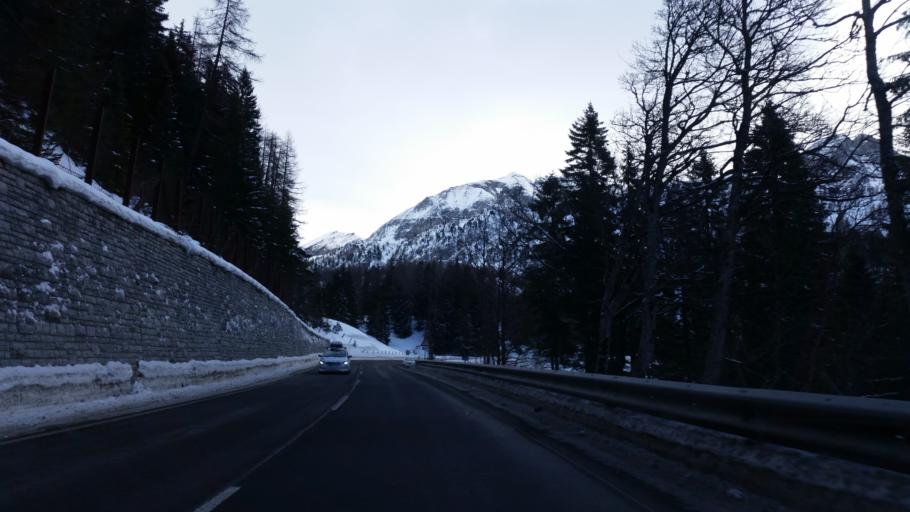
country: AT
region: Salzburg
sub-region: Politischer Bezirk Sankt Johann im Pongau
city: Untertauern
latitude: 47.2536
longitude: 13.5068
